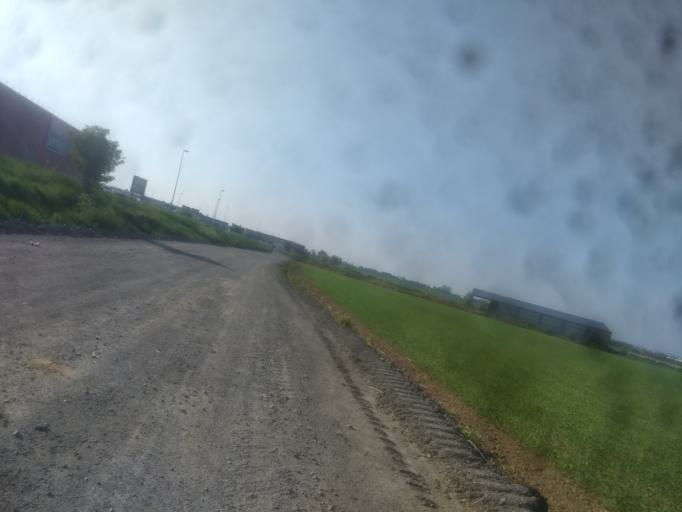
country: FR
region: Nord-Pas-de-Calais
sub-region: Departement du Pas-de-Calais
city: Beaurains
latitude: 50.2674
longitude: 2.8035
